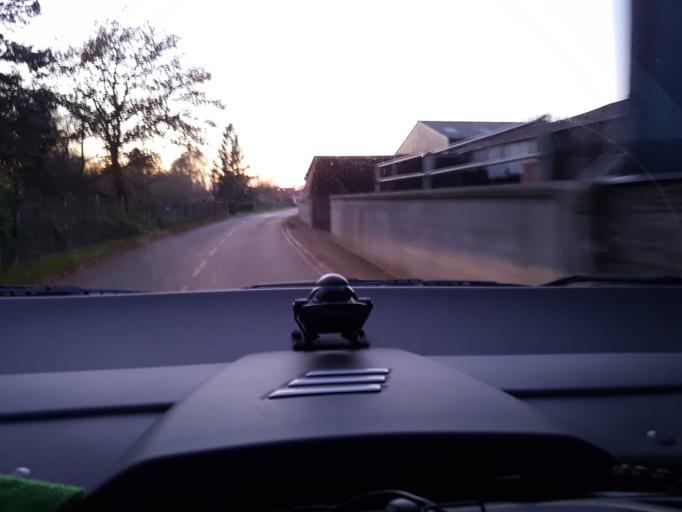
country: FR
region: Picardie
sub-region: Departement de la Somme
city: Rue
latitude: 50.2151
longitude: 1.7101
